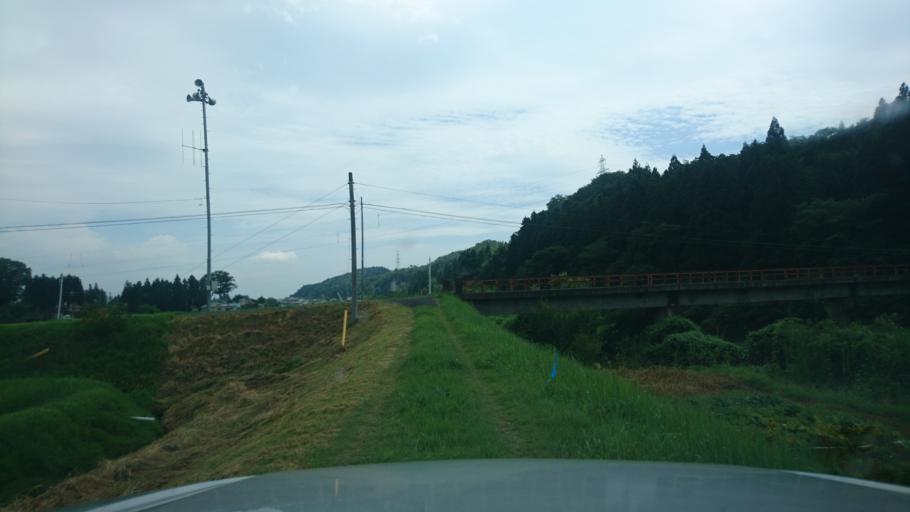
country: JP
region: Iwate
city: Ichinoseki
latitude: 38.8032
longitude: 140.9499
